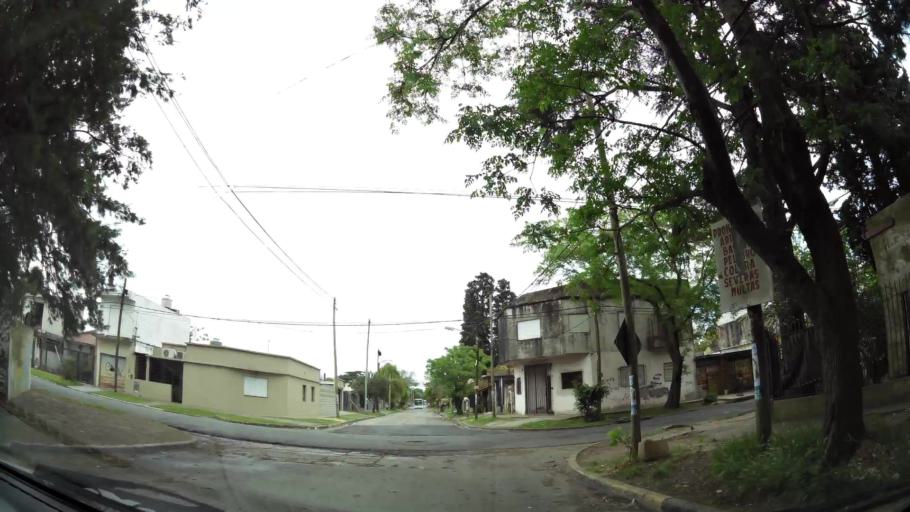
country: AR
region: Buenos Aires
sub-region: Partido de Quilmes
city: Quilmes
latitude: -34.7548
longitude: -58.2294
